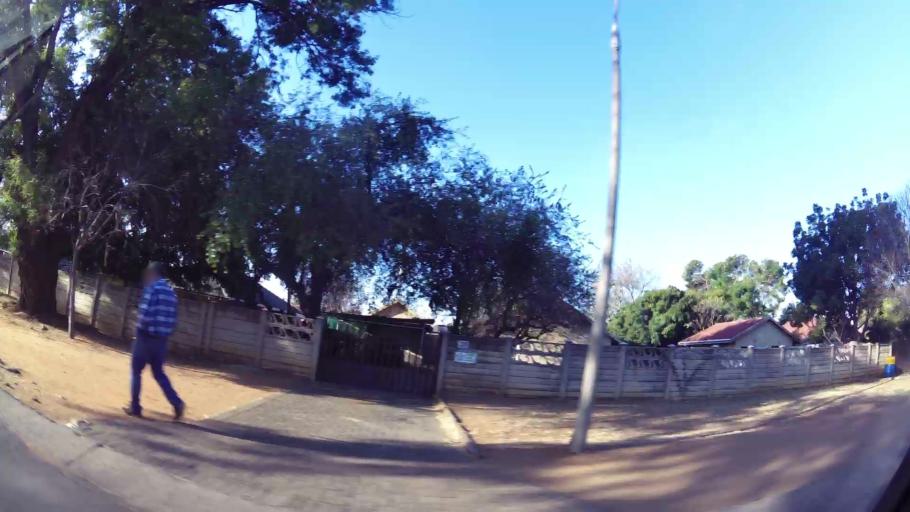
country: ZA
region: North-West
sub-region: Bojanala Platinum District Municipality
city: Rustenburg
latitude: -25.6811
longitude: 27.2169
